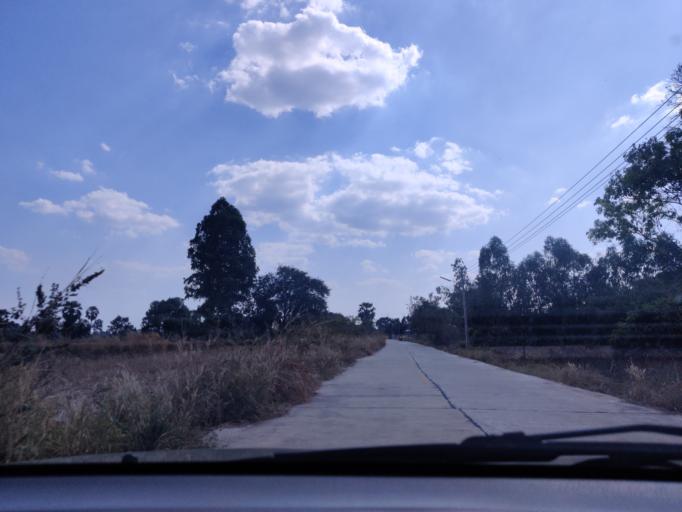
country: TH
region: Sisaket
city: Si Sa Ket
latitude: 15.0945
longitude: 104.3549
